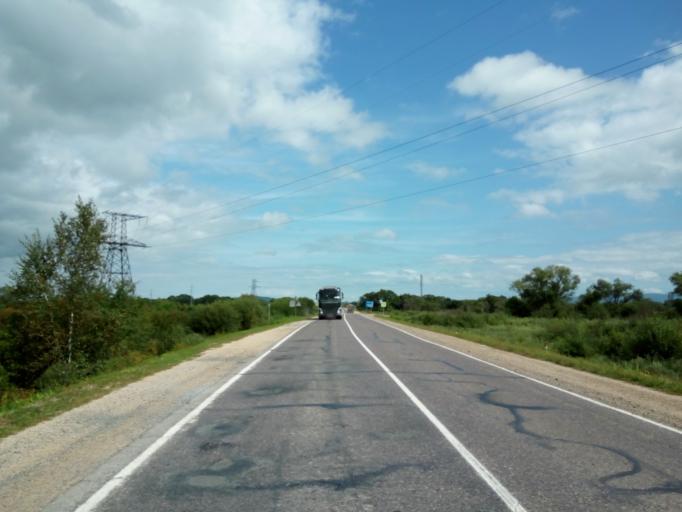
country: RU
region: Primorskiy
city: Dal'nerechensk
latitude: 45.9672
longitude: 133.7834
